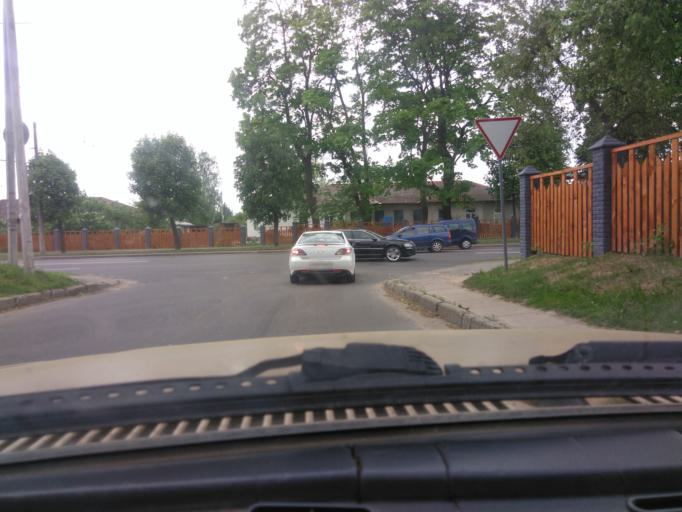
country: BY
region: Mogilev
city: Mahilyow
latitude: 53.9302
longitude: 30.3383
